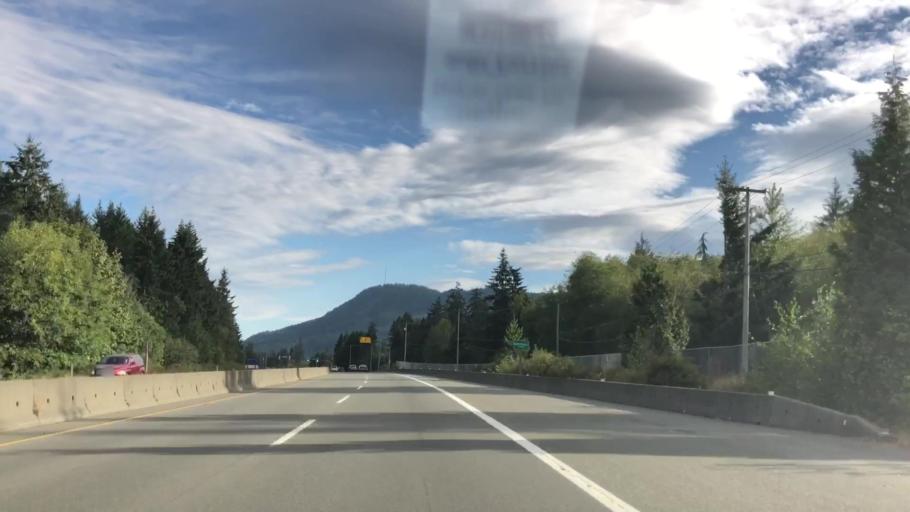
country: CA
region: British Columbia
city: North Saanich
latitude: 48.6302
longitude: -123.5489
